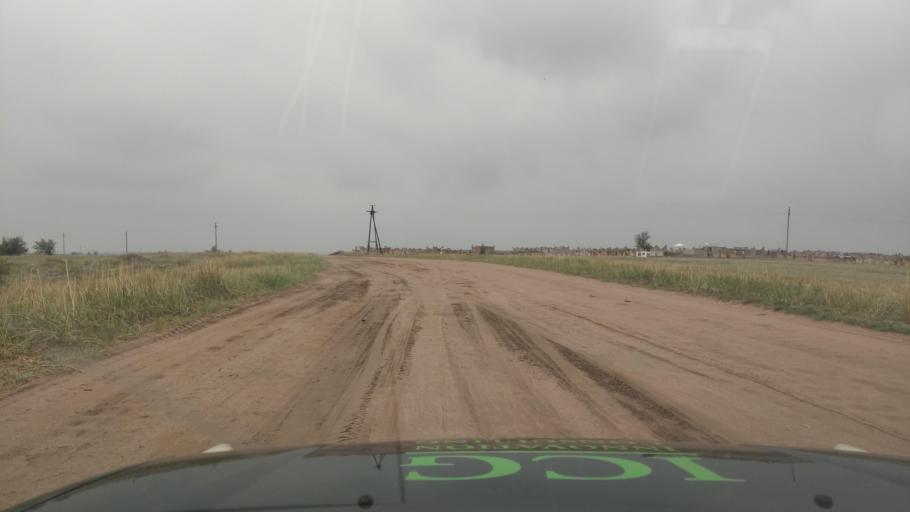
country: KZ
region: Pavlodar
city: Aksu
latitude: 52.0574
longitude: 77.1482
